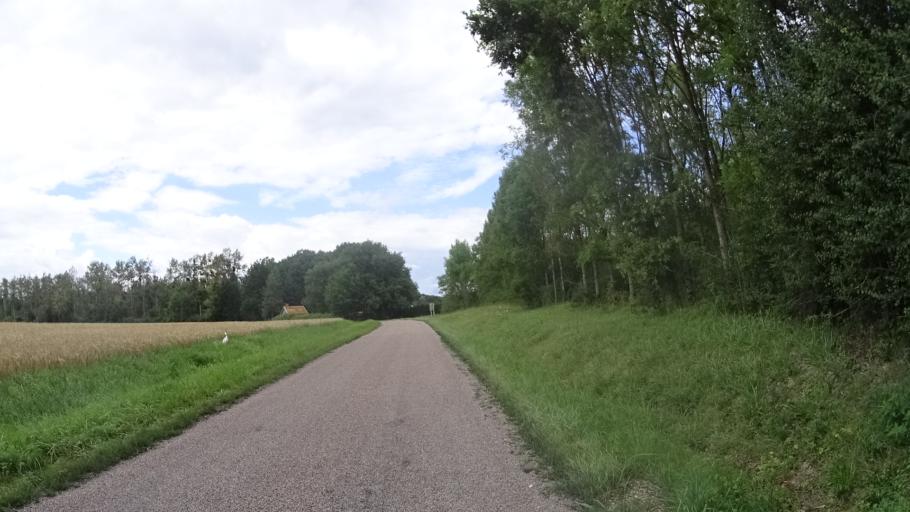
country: FR
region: Champagne-Ardenne
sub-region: Departement de la Haute-Marne
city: Villiers-en-Lieu
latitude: 48.6037
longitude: 4.8602
